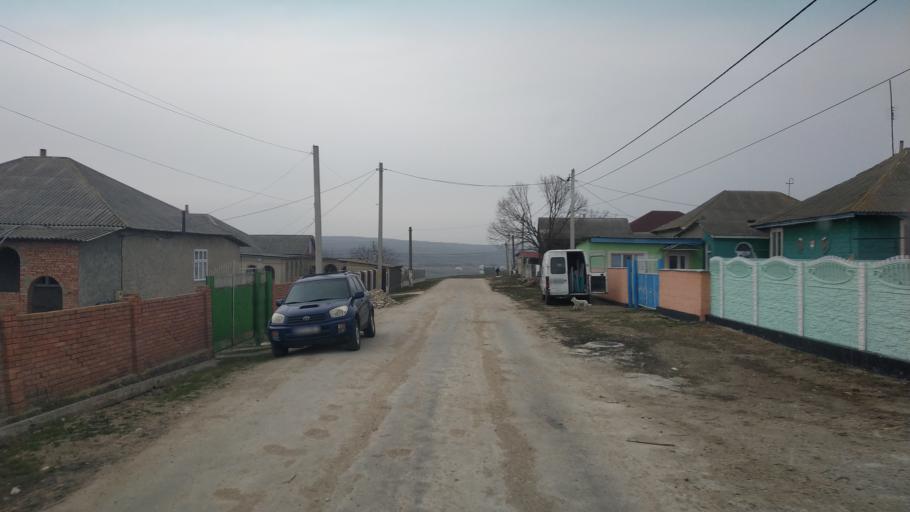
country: MD
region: Chisinau
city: Singera
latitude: 46.8254
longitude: 28.9632
